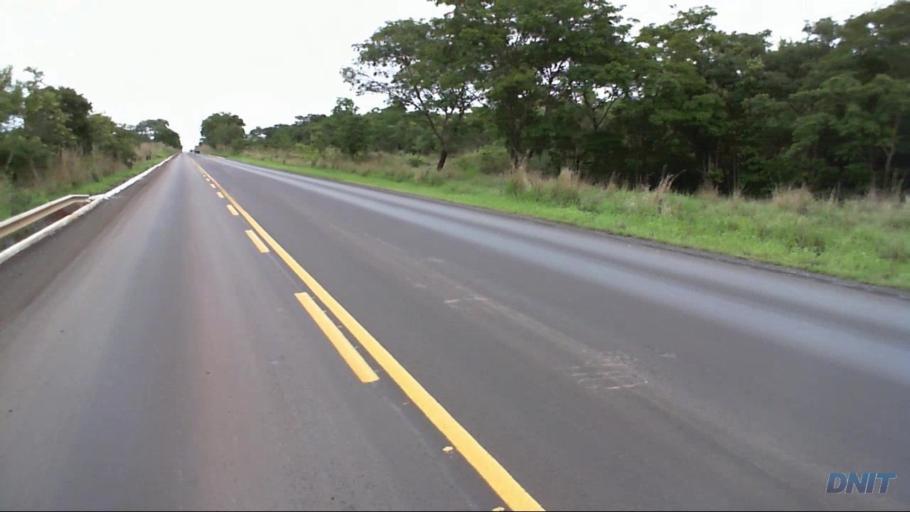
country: BR
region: Goias
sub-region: Padre Bernardo
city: Padre Bernardo
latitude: -15.1776
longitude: -48.4139
